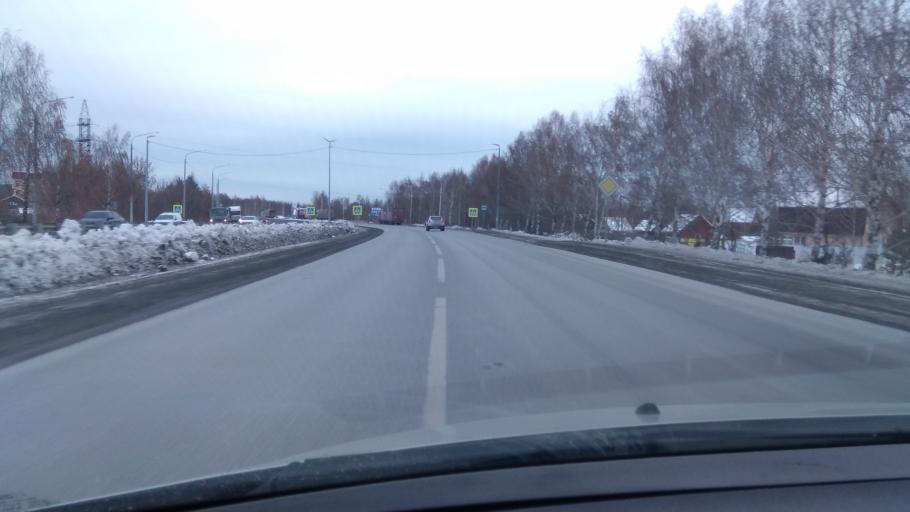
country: RU
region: Sverdlovsk
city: Aramil
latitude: 56.7027
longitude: 60.7486
